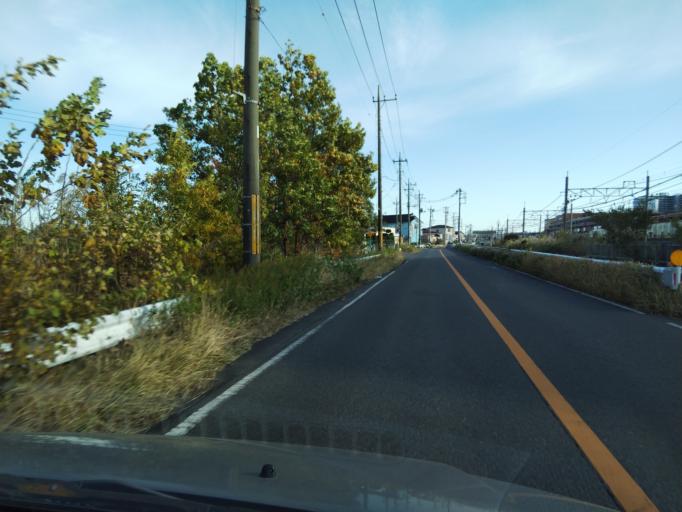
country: JP
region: Saitama
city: Yoshikawa
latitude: 35.8636
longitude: 139.8639
